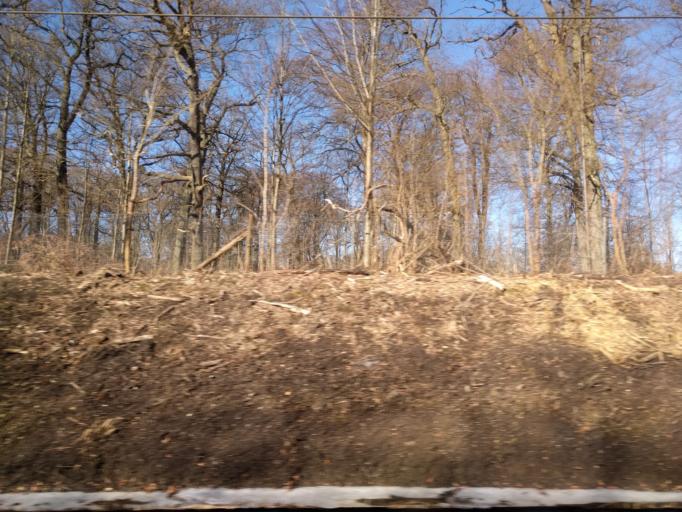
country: DK
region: Capital Region
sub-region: Gentofte Kommune
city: Charlottenlund
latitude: 55.7806
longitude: 12.5859
